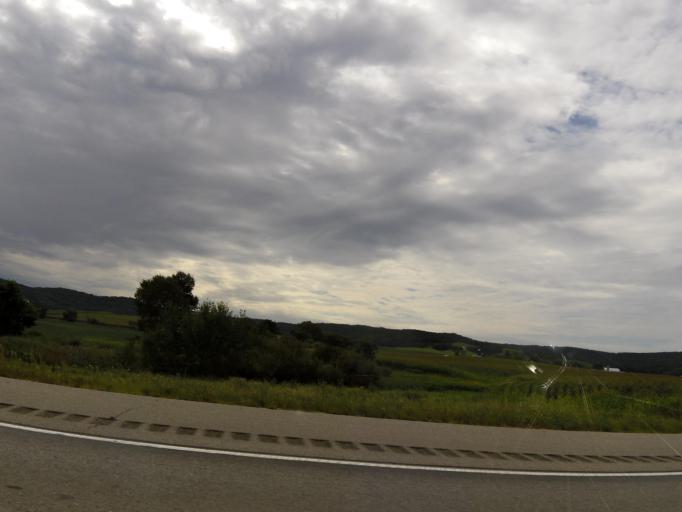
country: US
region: Wisconsin
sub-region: La Crosse County
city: Bangor
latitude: 43.8888
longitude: -90.9613
